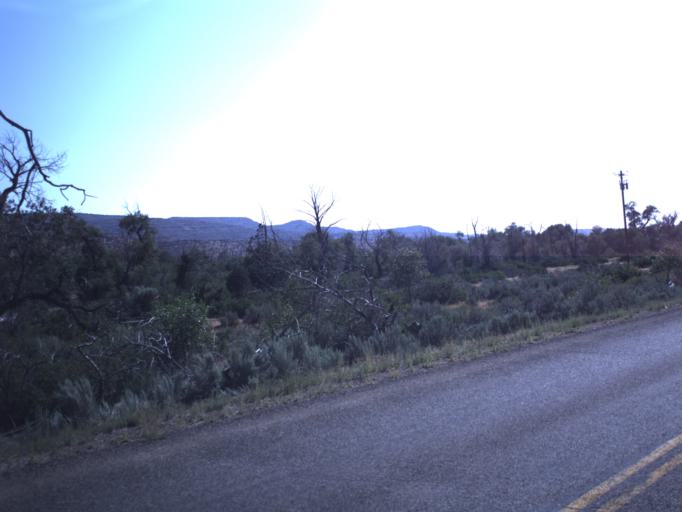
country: US
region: Utah
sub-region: Duchesne County
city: Duchesne
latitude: 40.2851
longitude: -110.4934
